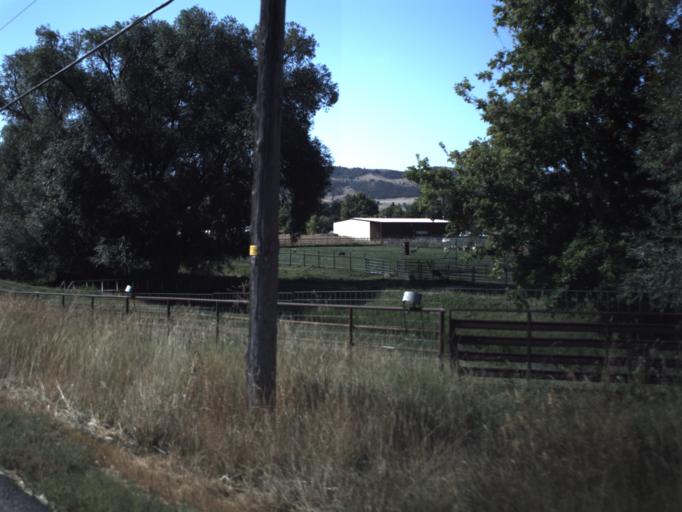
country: US
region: Utah
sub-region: Cache County
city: Hyrum
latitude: 41.5770
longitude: -111.8385
